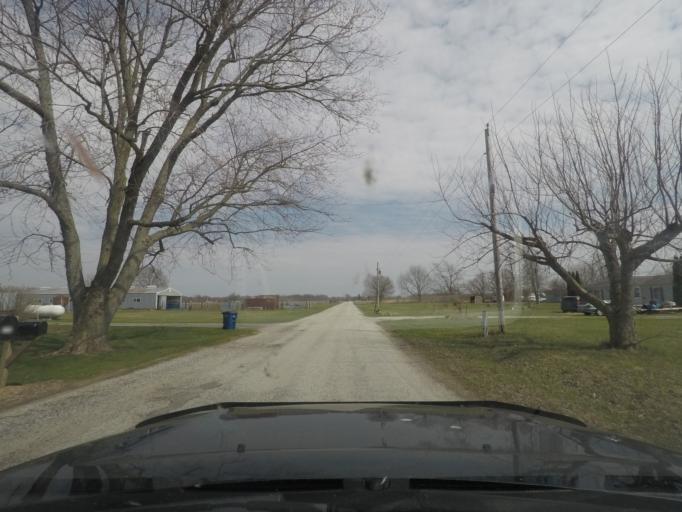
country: US
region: Indiana
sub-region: LaPorte County
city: Kingsford Heights
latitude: 41.4728
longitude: -86.6705
